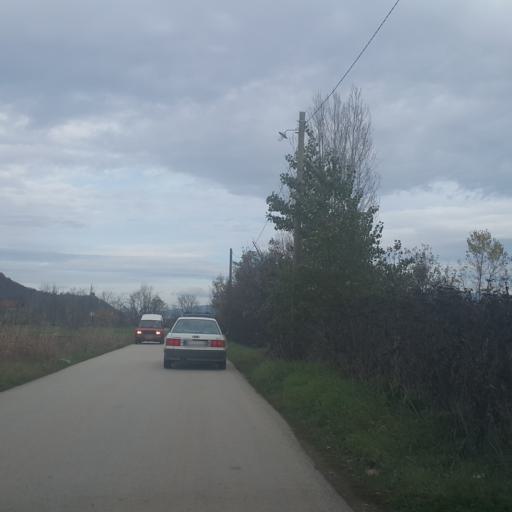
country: RS
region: Central Serbia
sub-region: Zajecarski Okrug
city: Knjazevac
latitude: 43.5835
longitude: 22.2491
